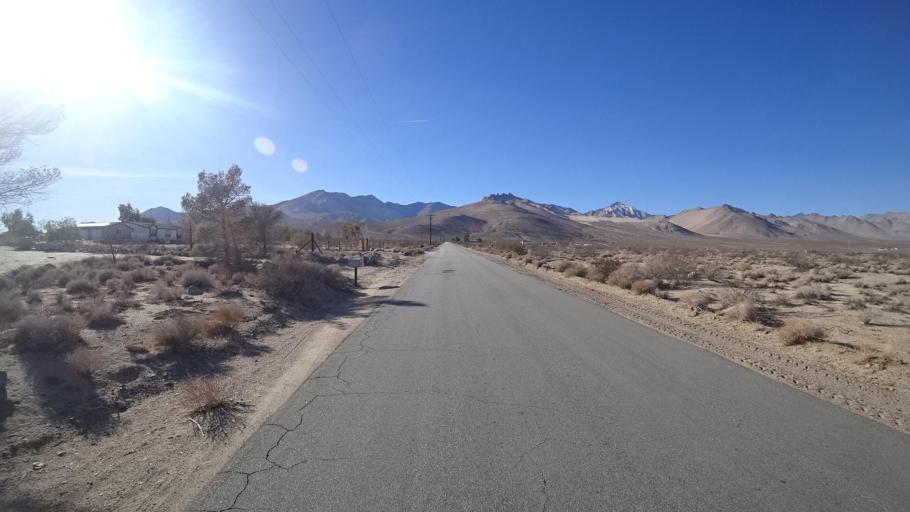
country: US
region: California
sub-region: Kern County
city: Inyokern
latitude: 35.6812
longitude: -117.8535
